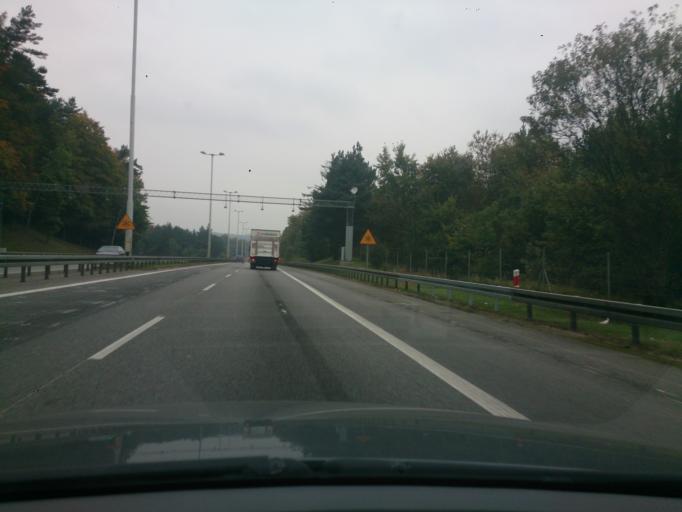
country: PL
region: Pomeranian Voivodeship
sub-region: Gdynia
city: Wielki Kack
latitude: 54.4672
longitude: 18.4789
